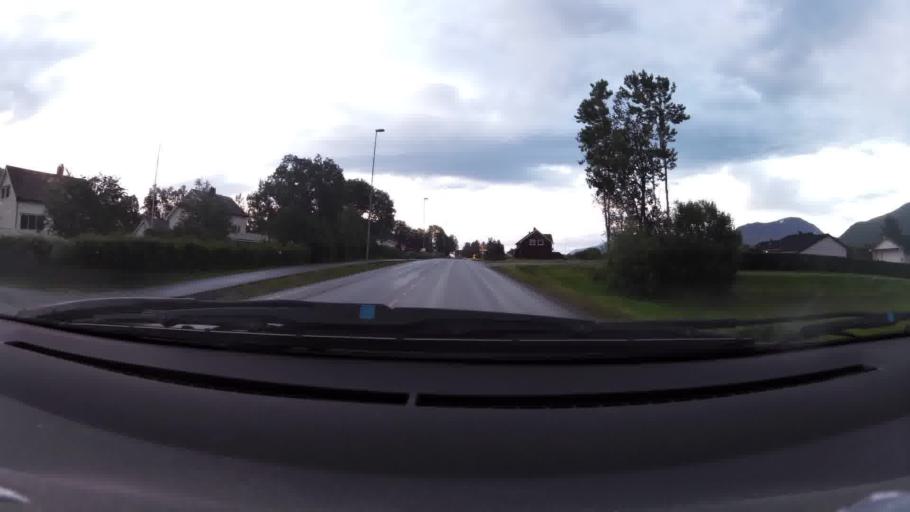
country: NO
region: More og Romsdal
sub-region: Eide
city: Eide
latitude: 62.9111
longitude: 7.4361
